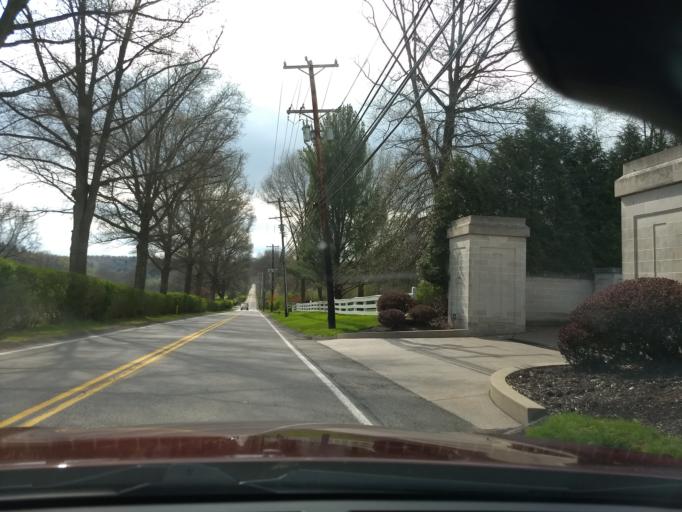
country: US
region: Pennsylvania
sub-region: Allegheny County
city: Fox Chapel
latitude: 40.5282
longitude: -79.8768
